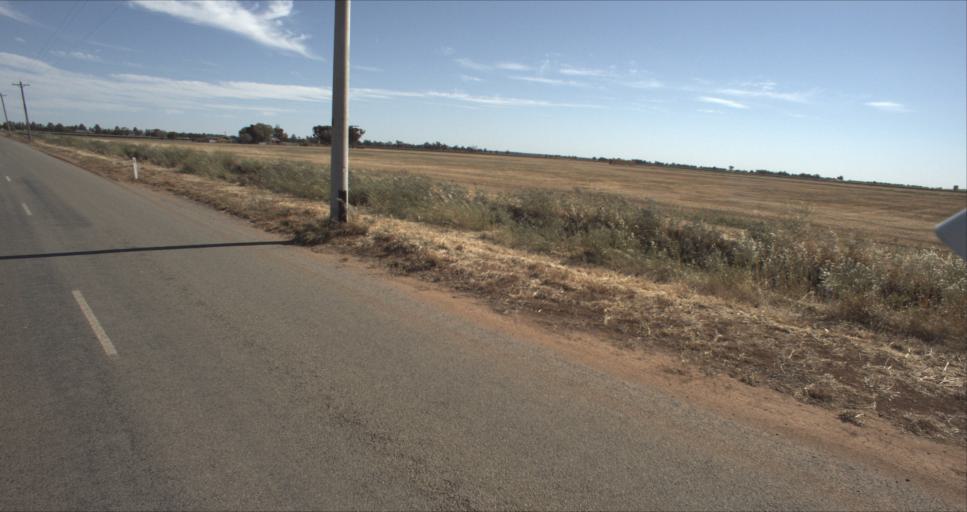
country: AU
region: New South Wales
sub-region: Leeton
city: Leeton
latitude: -34.5738
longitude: 146.3812
